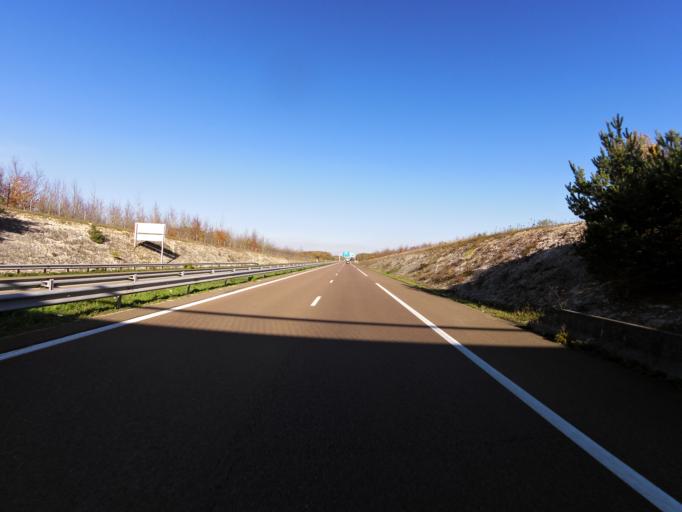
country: FR
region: Champagne-Ardenne
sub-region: Departement de la Marne
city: Fagnieres
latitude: 48.9001
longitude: 4.2860
